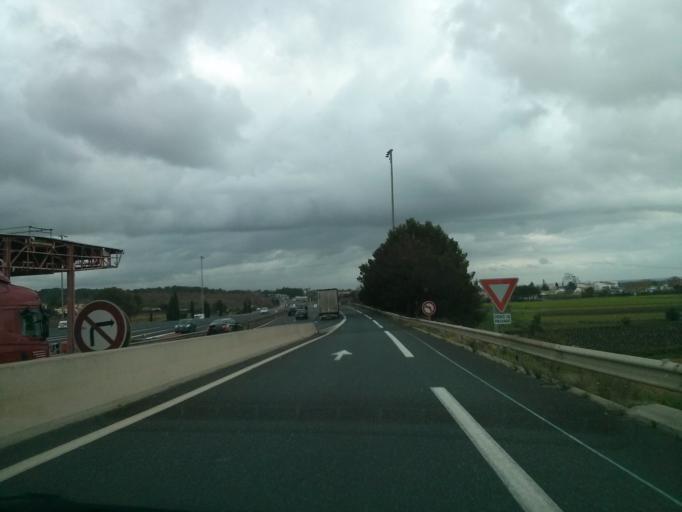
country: FR
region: Languedoc-Roussillon
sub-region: Departement du Gard
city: Aigues-Vives
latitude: 43.7263
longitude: 4.1828
